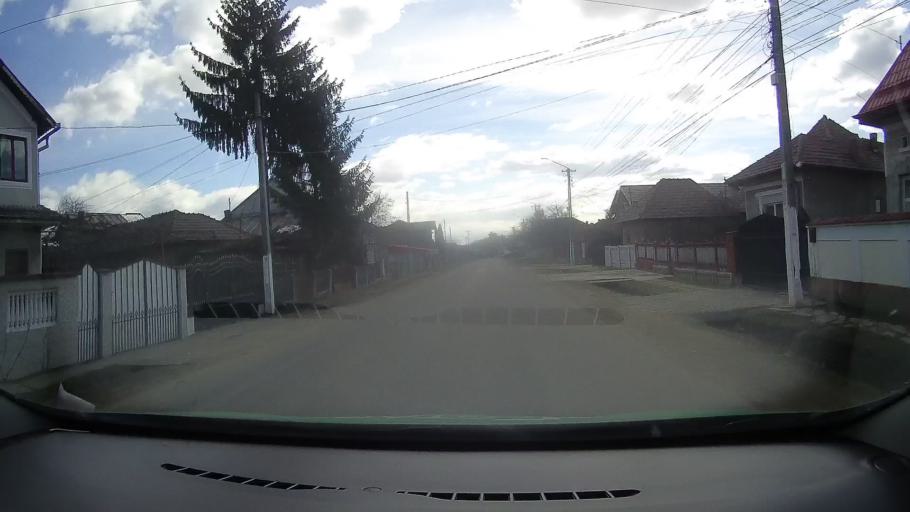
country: RO
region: Dambovita
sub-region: Comuna Doicesti
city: Doicesti
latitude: 44.9783
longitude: 25.3913
